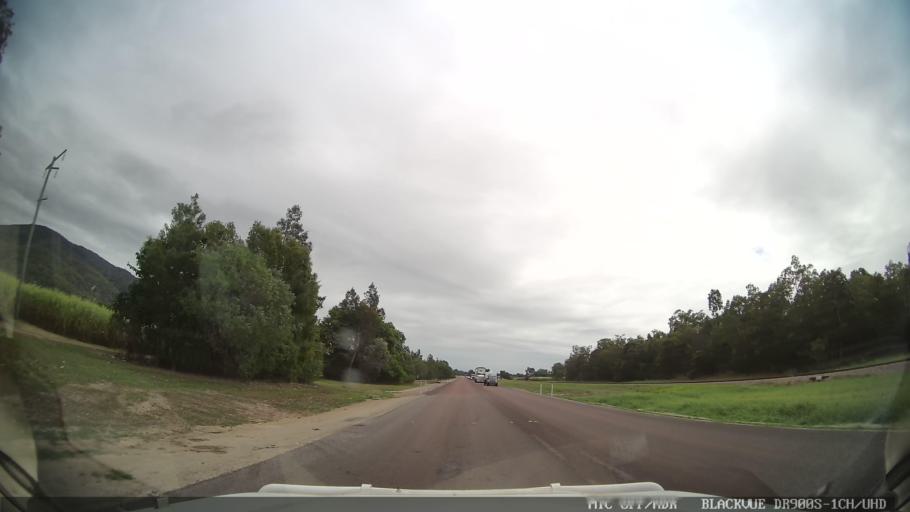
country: AU
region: Queensland
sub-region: Hinchinbrook
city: Ingham
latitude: -18.9264
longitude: 146.2633
